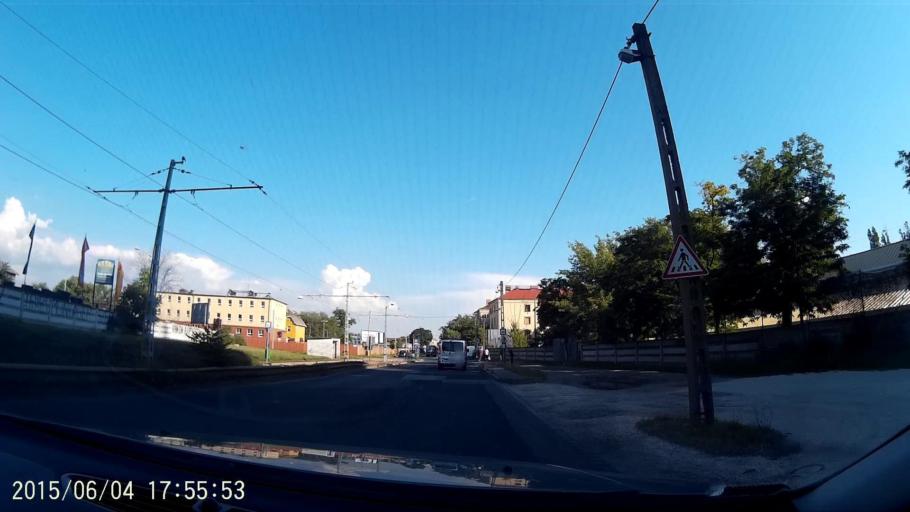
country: HU
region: Budapest
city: Budapest XX. keruelet
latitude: 47.4571
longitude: 19.0891
